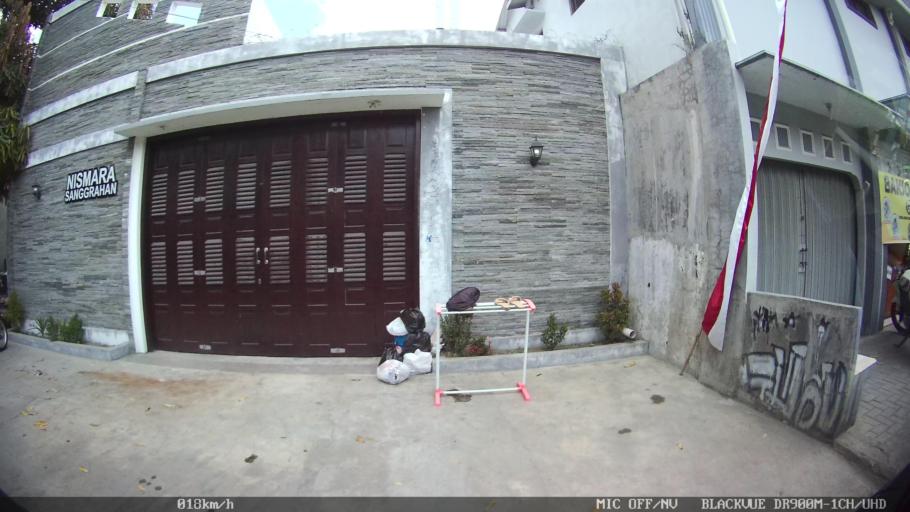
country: ID
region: Daerah Istimewa Yogyakarta
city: Kasihan
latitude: -7.8109
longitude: 110.3420
